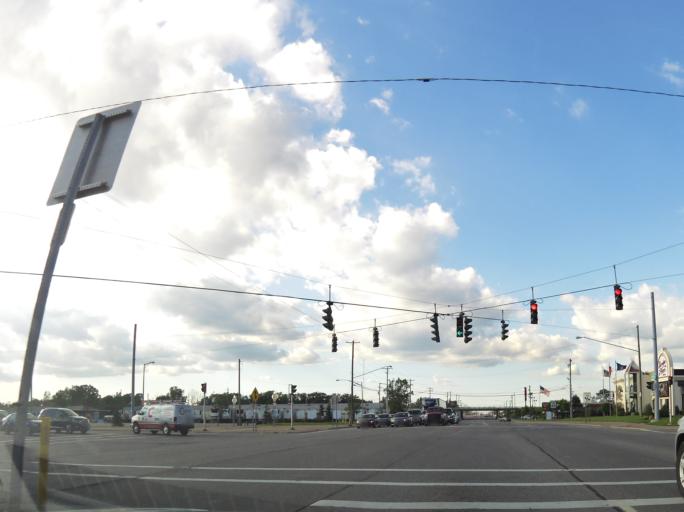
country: US
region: New York
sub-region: Erie County
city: Harris Hill
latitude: 42.9466
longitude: -78.6968
